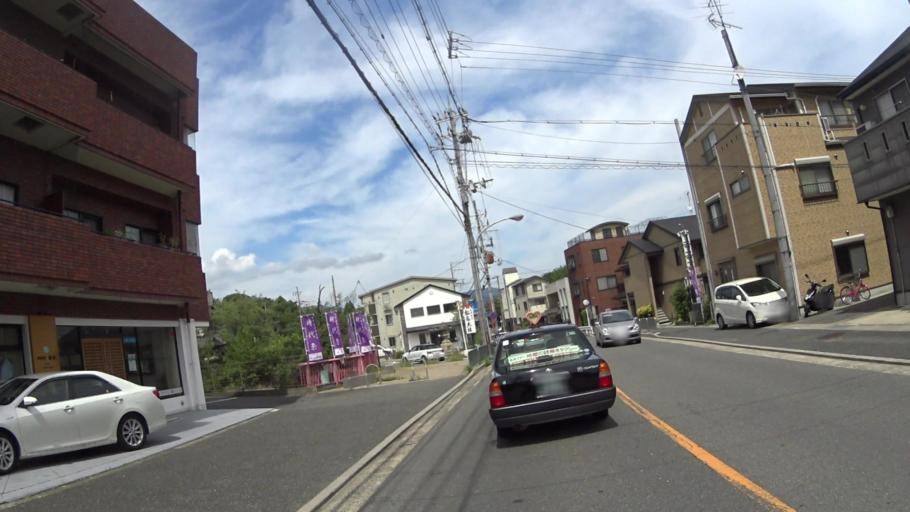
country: JP
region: Kyoto
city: Muko
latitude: 34.9989
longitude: 135.6882
